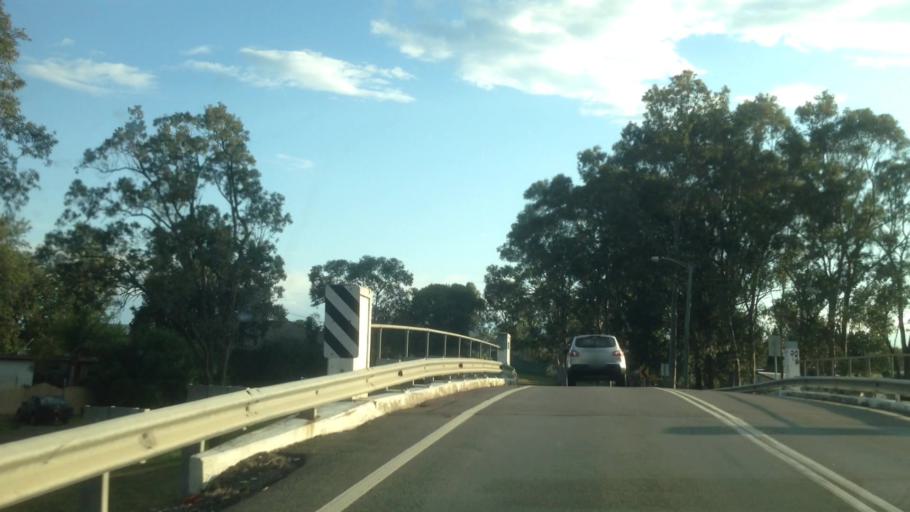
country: AU
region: New South Wales
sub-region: Cessnock
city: Kurri Kurri
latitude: -32.8266
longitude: 151.4823
